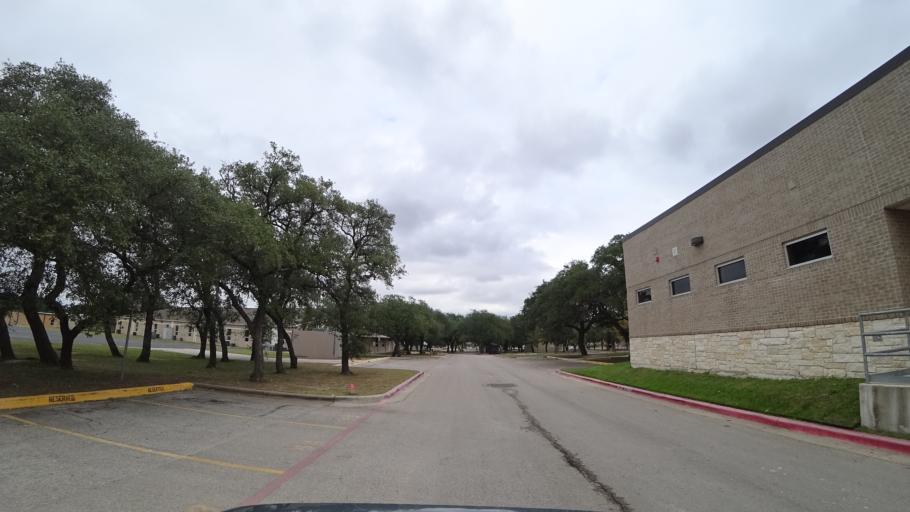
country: US
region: Texas
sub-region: Williamson County
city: Round Rock
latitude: 30.5103
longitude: -97.6980
